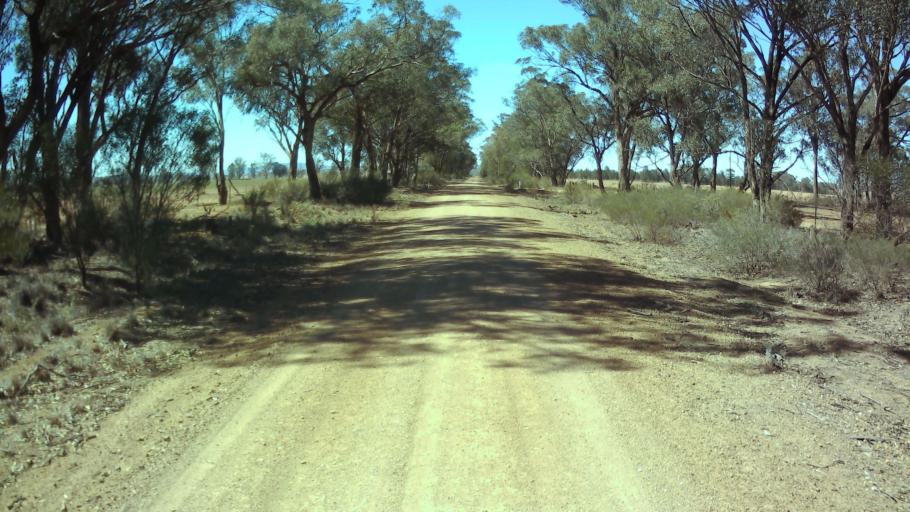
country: AU
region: New South Wales
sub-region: Weddin
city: Grenfell
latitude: -33.7114
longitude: 147.9705
